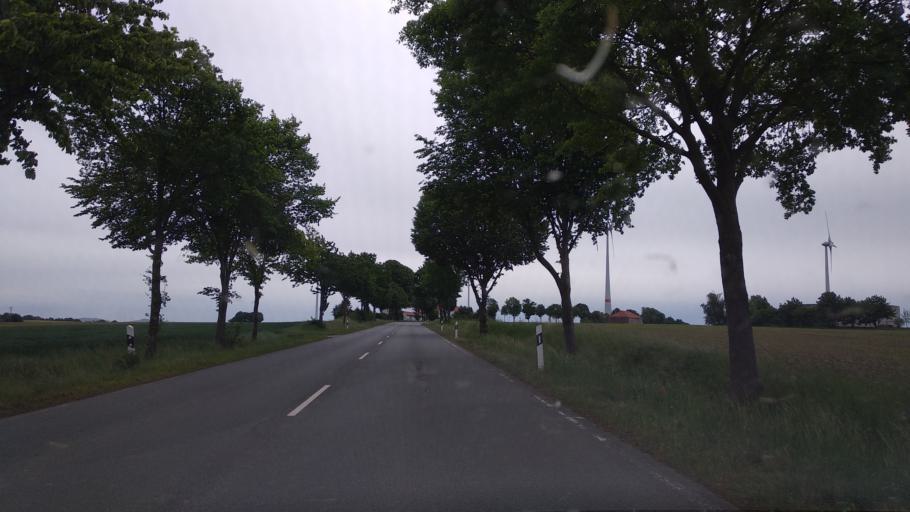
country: DE
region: North Rhine-Westphalia
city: Borgentreich
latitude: 51.5897
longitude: 9.1463
